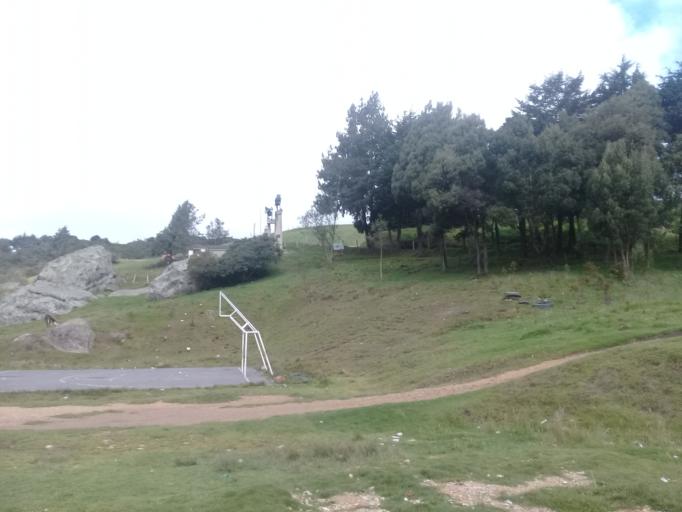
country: CO
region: Boyaca
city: Samaca
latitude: 5.4445
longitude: -73.4385
